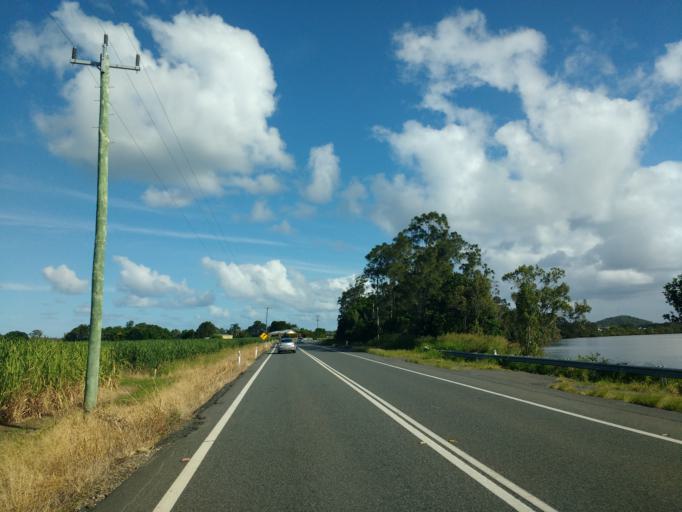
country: AU
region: New South Wales
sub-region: Richmond Valley
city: Evans Head
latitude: -28.9901
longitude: 153.4624
